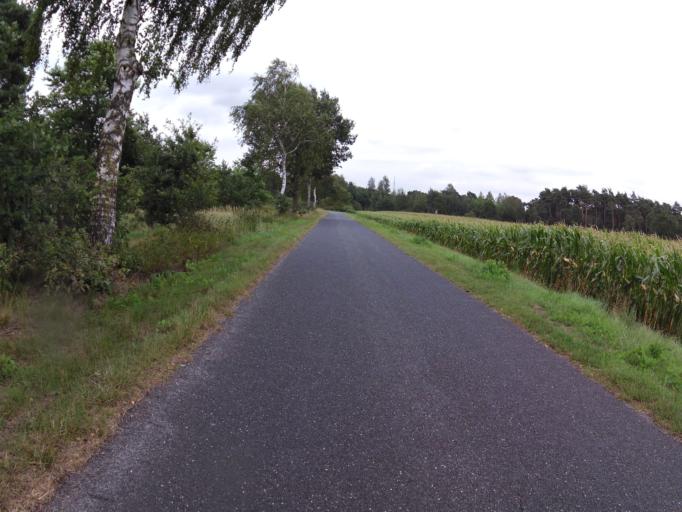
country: DE
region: Lower Saxony
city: Rotenburg
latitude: 53.1345
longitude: 9.4414
